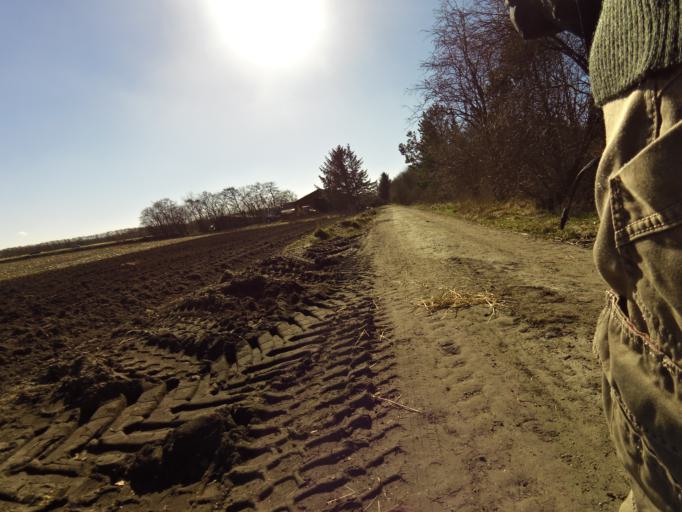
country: DK
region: South Denmark
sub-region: Varde Kommune
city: Varde
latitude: 55.5786
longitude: 8.4059
